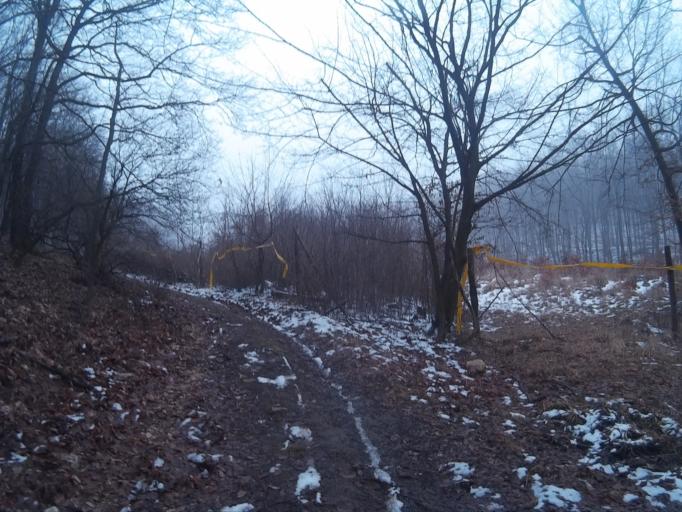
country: HU
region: Komarom-Esztergom
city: Tardos
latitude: 47.6668
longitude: 18.4717
